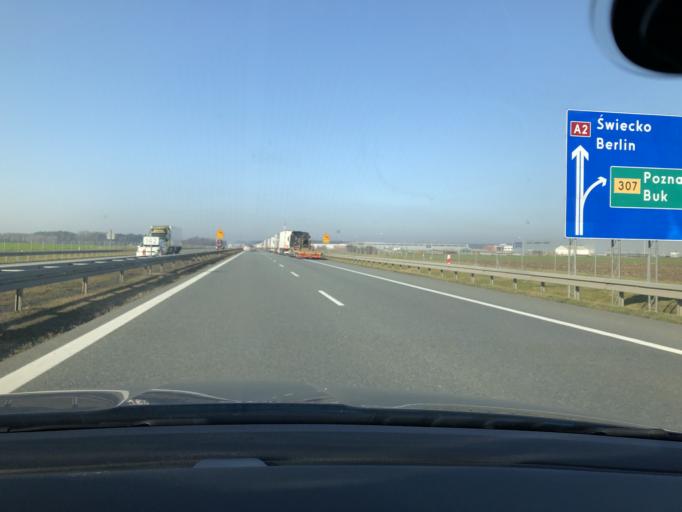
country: PL
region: Greater Poland Voivodeship
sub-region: Powiat poznanski
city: Buk
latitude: 52.3681
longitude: 16.5899
